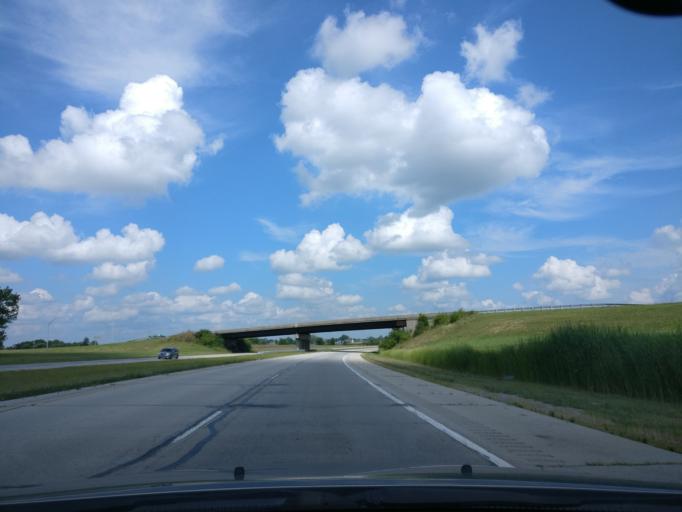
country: US
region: Ohio
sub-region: Greene County
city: Wilberforce
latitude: 39.6895
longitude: -83.8850
